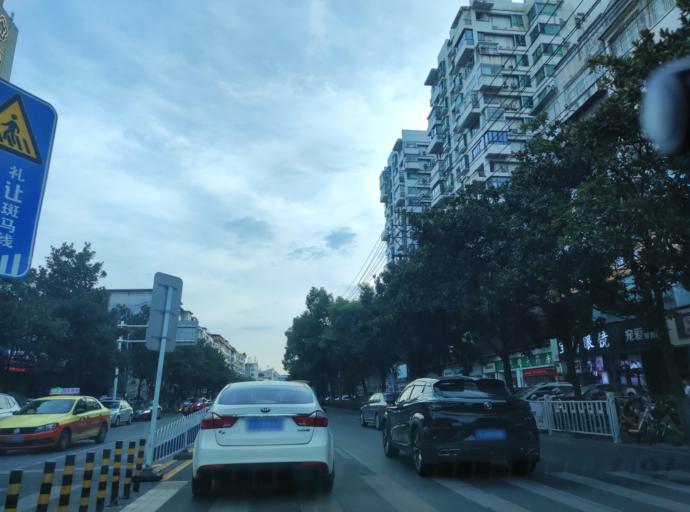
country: CN
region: Jiangxi Sheng
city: Pingxiang
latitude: 27.6343
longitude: 113.8561
